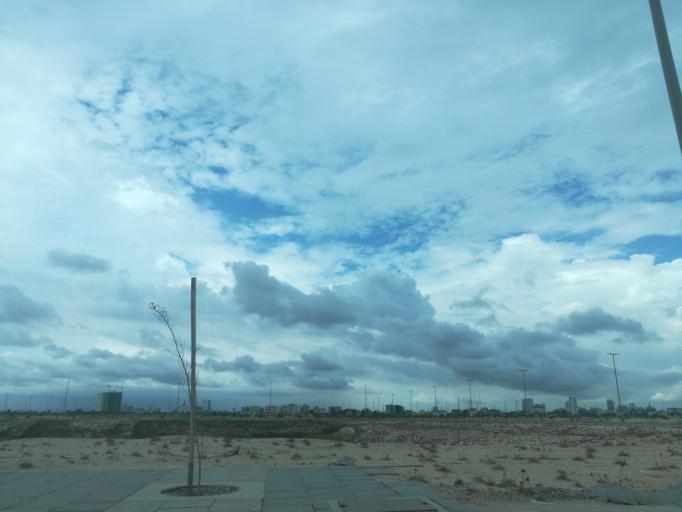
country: NG
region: Lagos
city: Ikoyi
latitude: 6.4061
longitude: 3.4206
